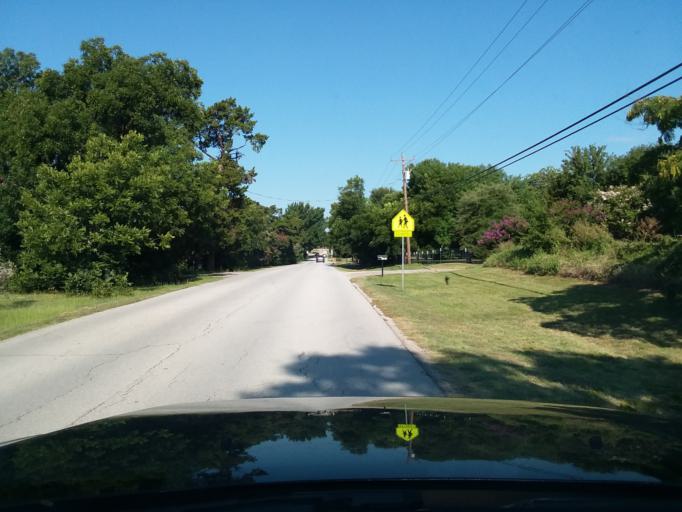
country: US
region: Texas
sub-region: Denton County
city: Double Oak
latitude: 33.0626
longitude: -97.0904
